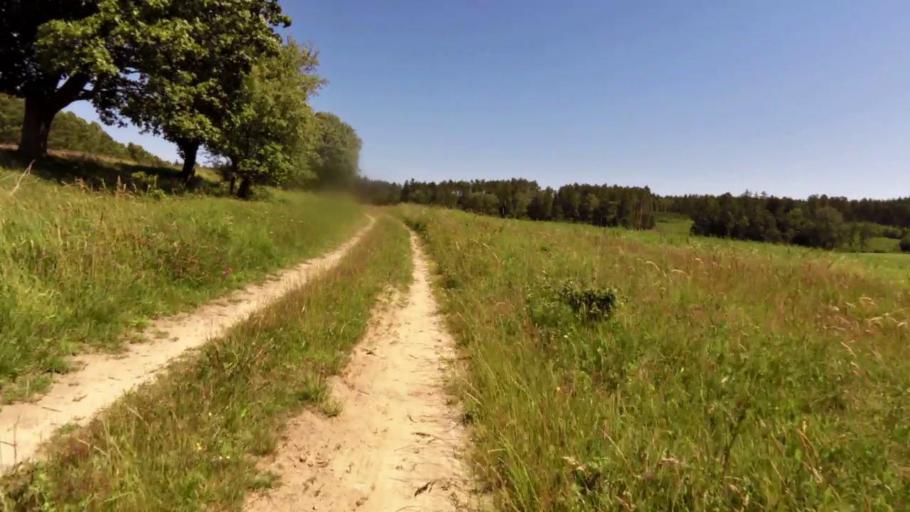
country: PL
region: West Pomeranian Voivodeship
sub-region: Powiat swidwinski
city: Polczyn-Zdroj
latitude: 53.9001
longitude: 16.0973
